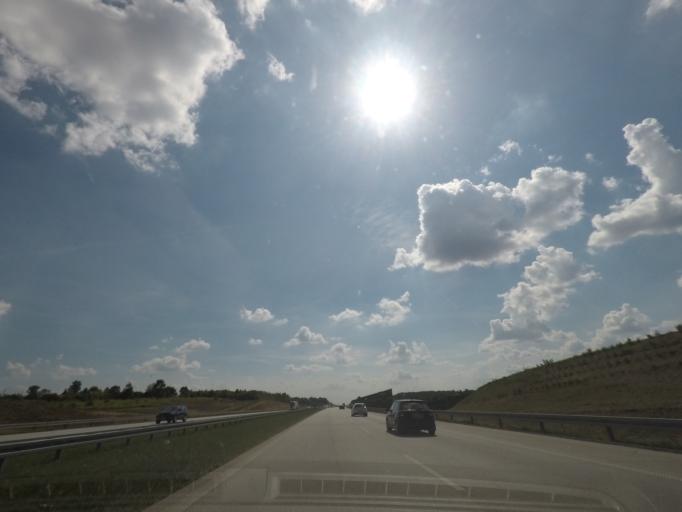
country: PL
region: Lodz Voivodeship
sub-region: Powiat zgierski
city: Strykow
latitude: 51.8195
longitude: 19.6448
